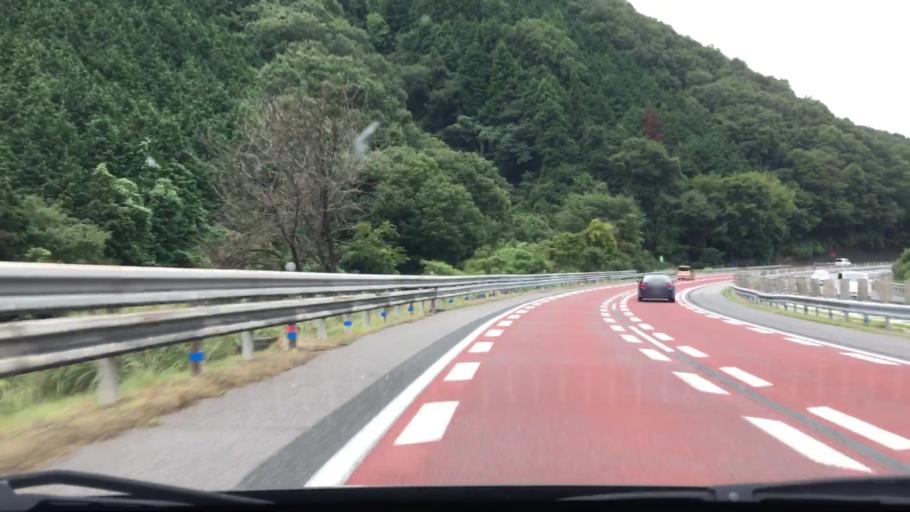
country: JP
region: Hiroshima
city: Miyoshi
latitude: 34.7804
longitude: 132.8439
